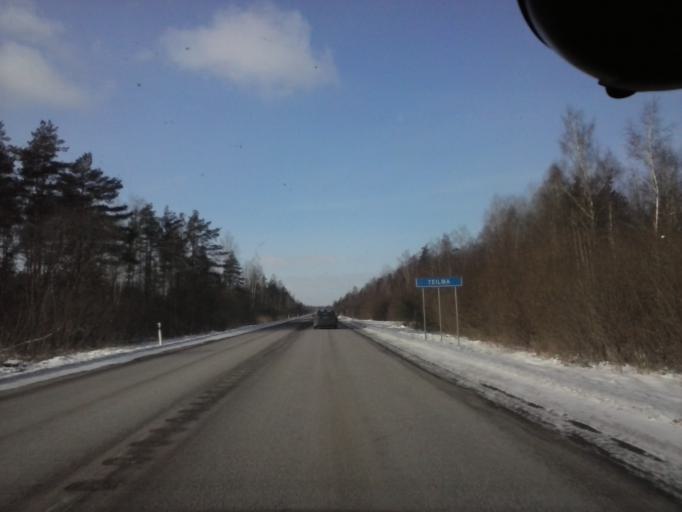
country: EE
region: Tartu
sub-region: Noo vald
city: Noo
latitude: 58.3453
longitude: 26.4821
